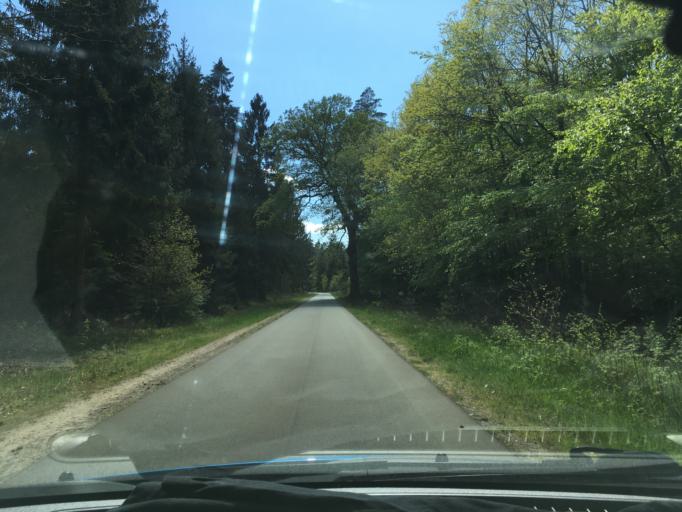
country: DE
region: Lower Saxony
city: Stoetze
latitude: 53.1076
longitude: 10.7840
